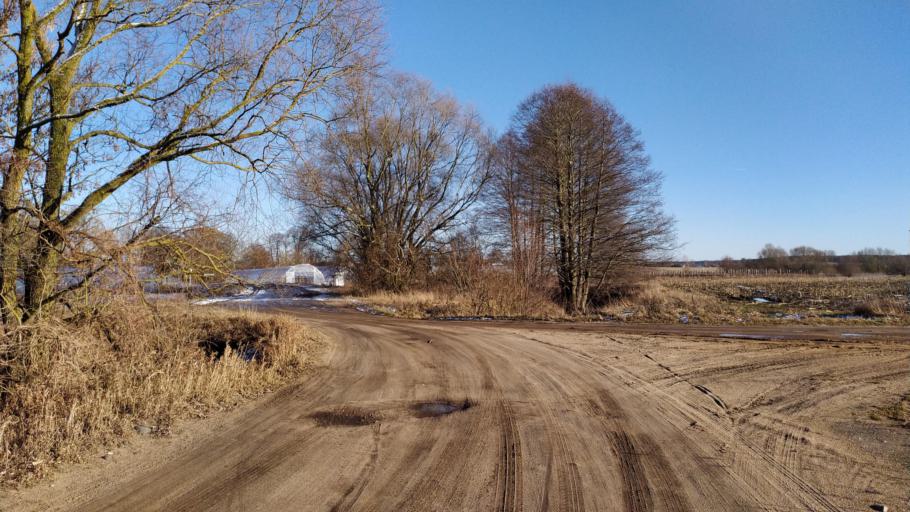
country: BY
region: Brest
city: Kamyanyets
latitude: 52.3720
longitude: 23.8928
